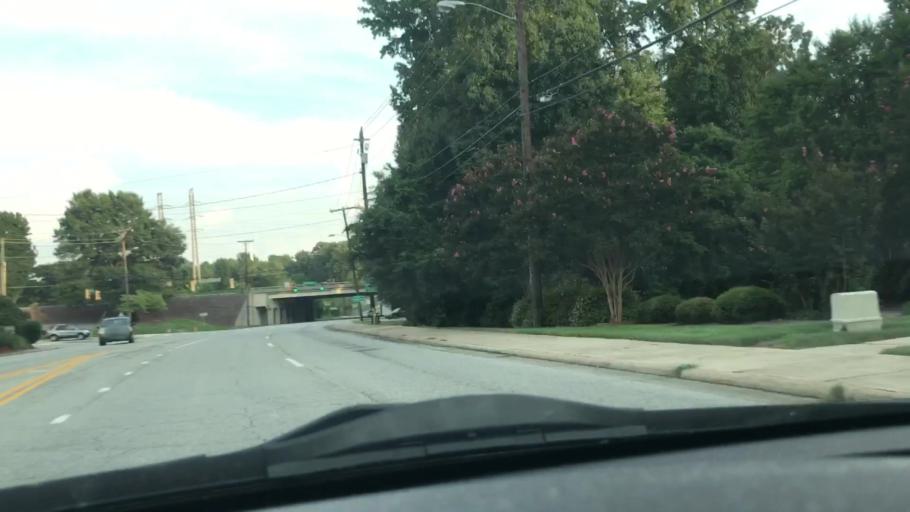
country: US
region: North Carolina
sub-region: Guilford County
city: Greensboro
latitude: 36.0833
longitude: -79.8320
